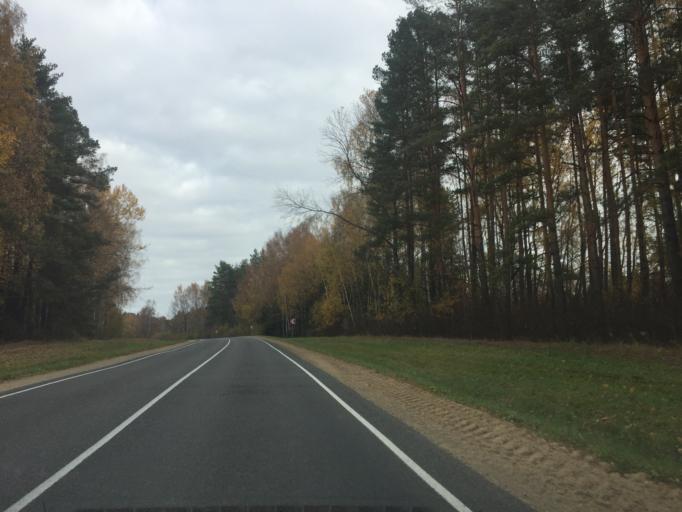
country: BY
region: Minsk
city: Svir
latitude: 54.8237
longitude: 26.1852
